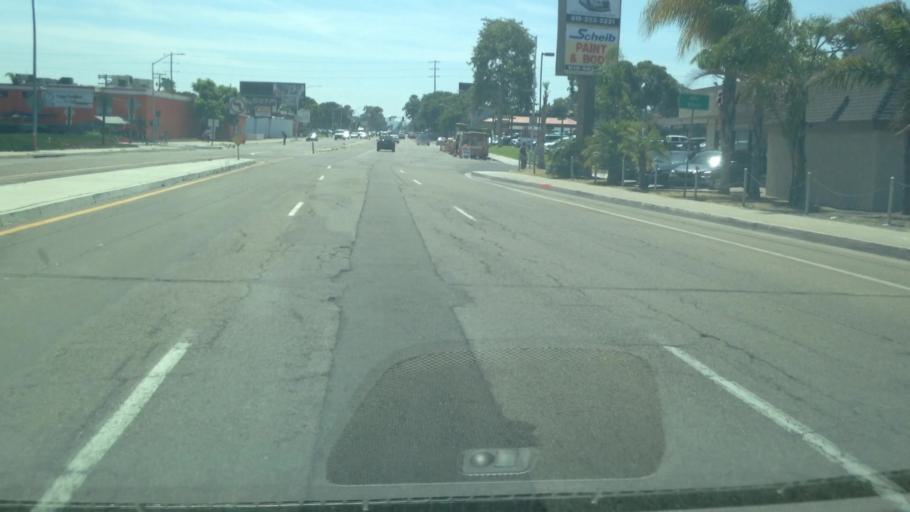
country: US
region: California
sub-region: San Diego County
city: San Diego
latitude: 32.7566
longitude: -117.2225
